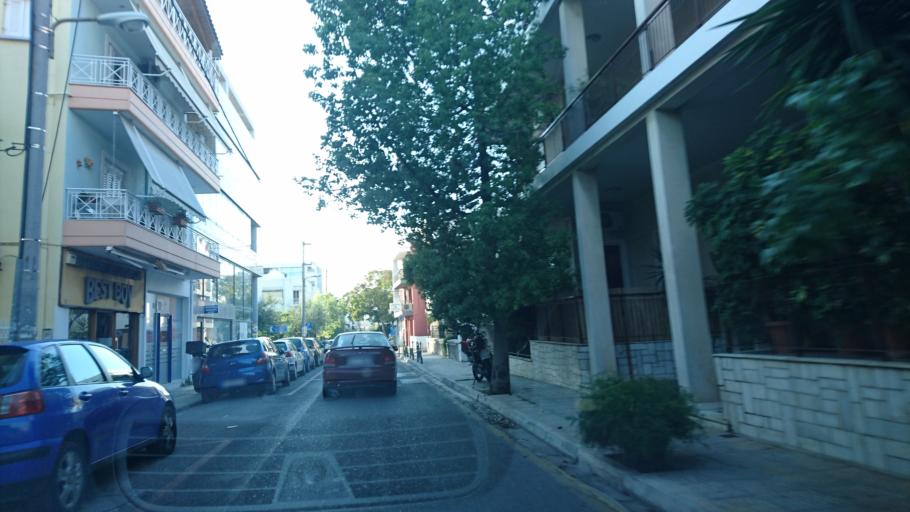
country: GR
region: Attica
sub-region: Nomarchia Athinas
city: Khalandrion
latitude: 38.0205
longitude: 23.8047
